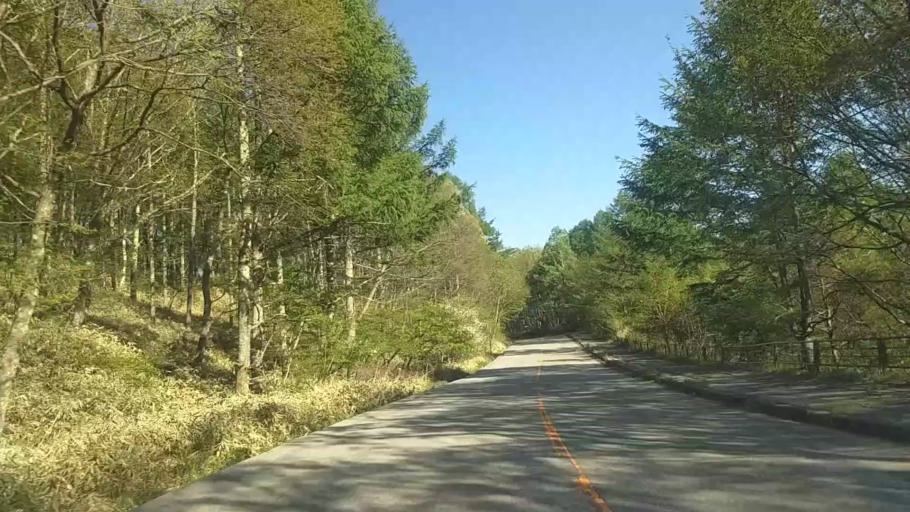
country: JP
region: Yamanashi
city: Nirasaki
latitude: 35.9068
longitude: 138.3917
